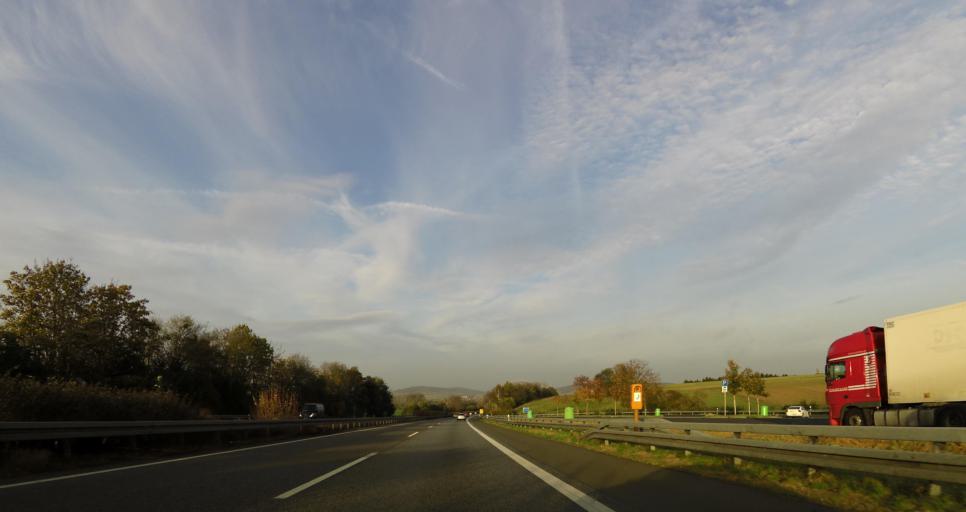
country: DE
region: Lower Saxony
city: Hillerse
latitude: 51.7174
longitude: 9.9428
